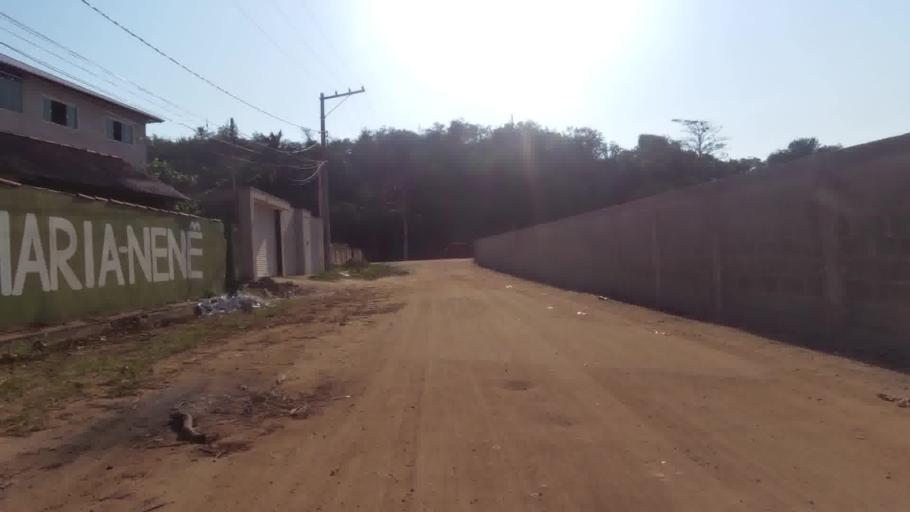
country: BR
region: Espirito Santo
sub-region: Piuma
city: Piuma
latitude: -20.8551
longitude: -40.7515
